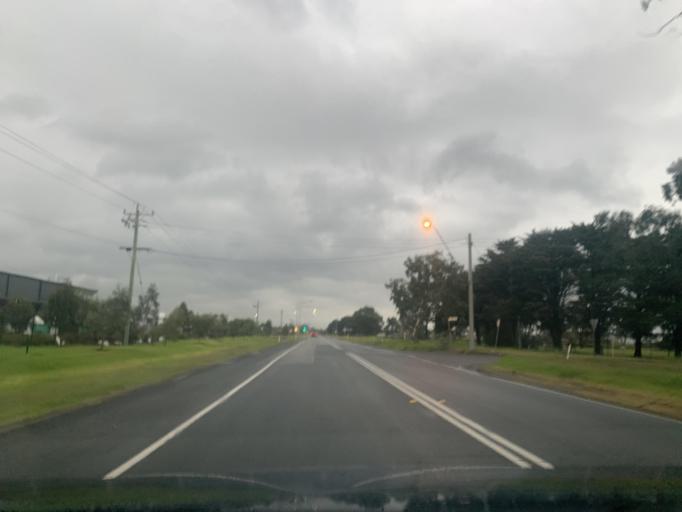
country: AU
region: Victoria
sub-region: Greater Dandenong
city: Keysborough
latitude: -38.0244
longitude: 145.1815
